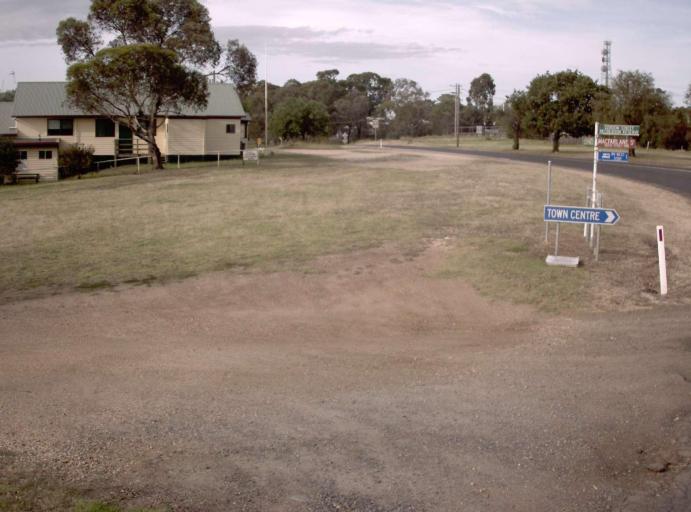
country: AU
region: Victoria
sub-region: Wellington
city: Heyfield
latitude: -37.9844
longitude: 146.7825
